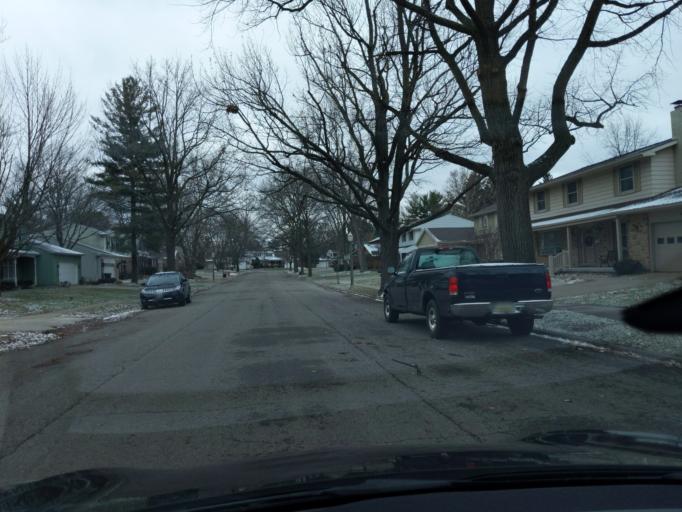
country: US
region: Michigan
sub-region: Ingham County
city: East Lansing
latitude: 42.7538
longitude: -84.5100
